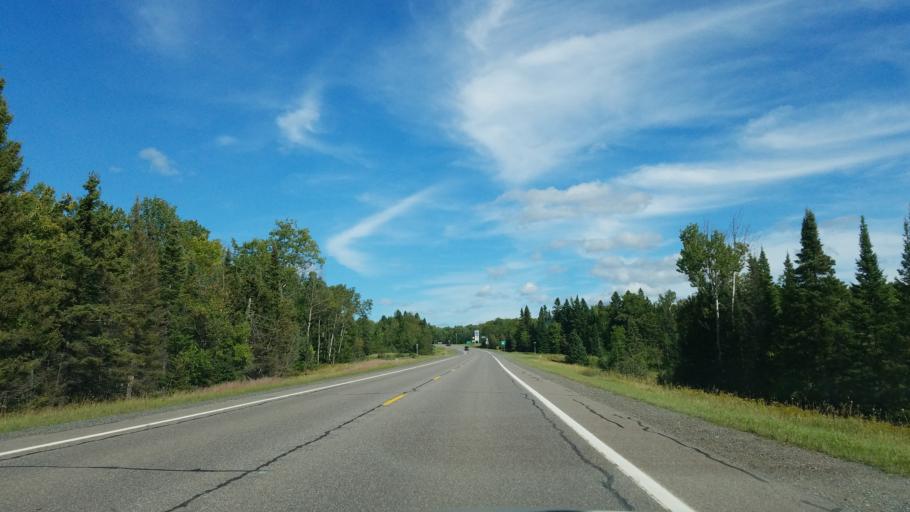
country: US
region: Michigan
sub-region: Baraga County
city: L'Anse
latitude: 46.5456
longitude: -88.5453
